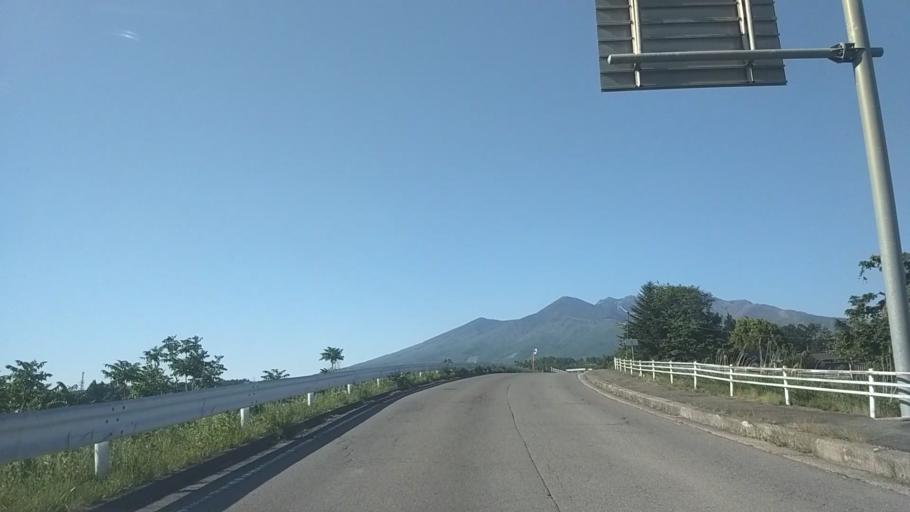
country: JP
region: Nagano
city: Chino
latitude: 35.8643
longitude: 138.3116
